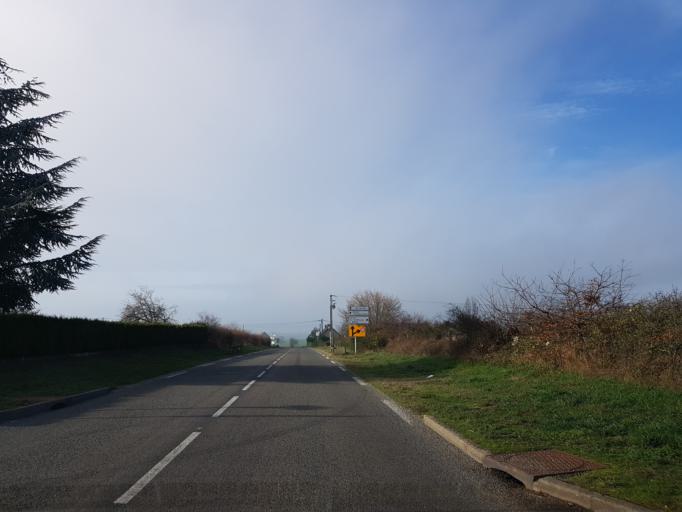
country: FR
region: Bourgogne
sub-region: Departement de Saone-et-Loire
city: Gueugnon
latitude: 46.5978
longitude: 3.9964
